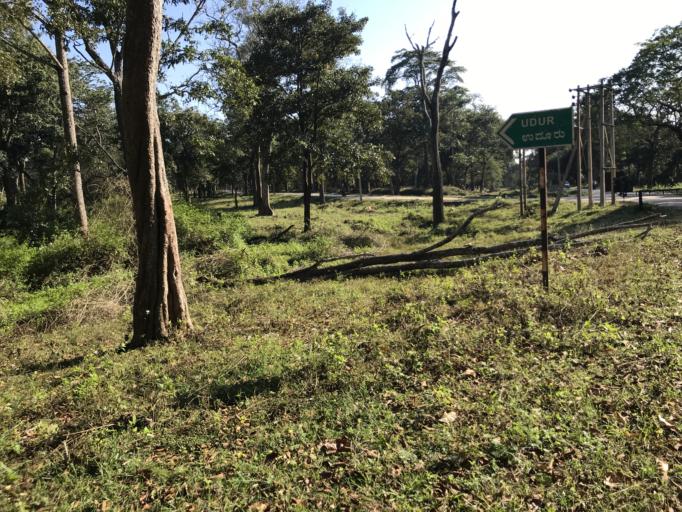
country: IN
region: Karnataka
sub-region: Mysore
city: Heggadadevankote
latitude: 11.9537
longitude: 76.2282
